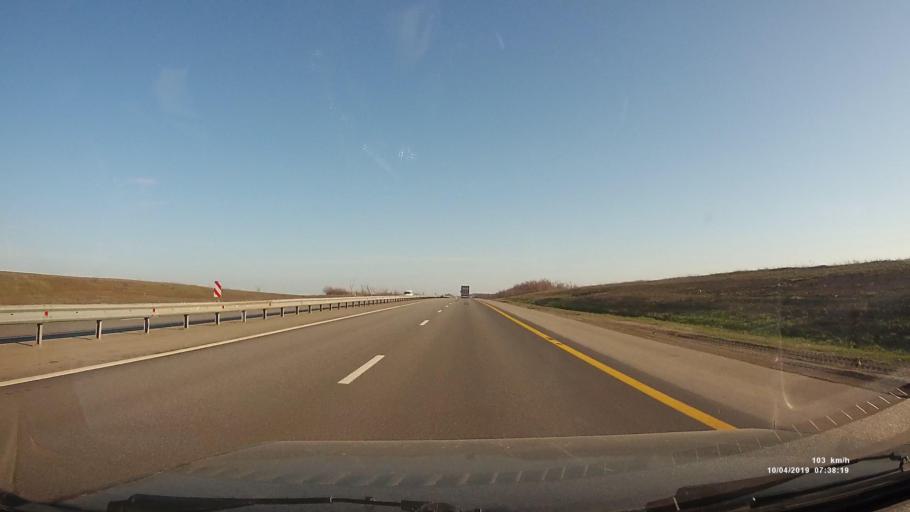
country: RU
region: Rostov
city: Likhoy
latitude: 48.0870
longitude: 40.2596
